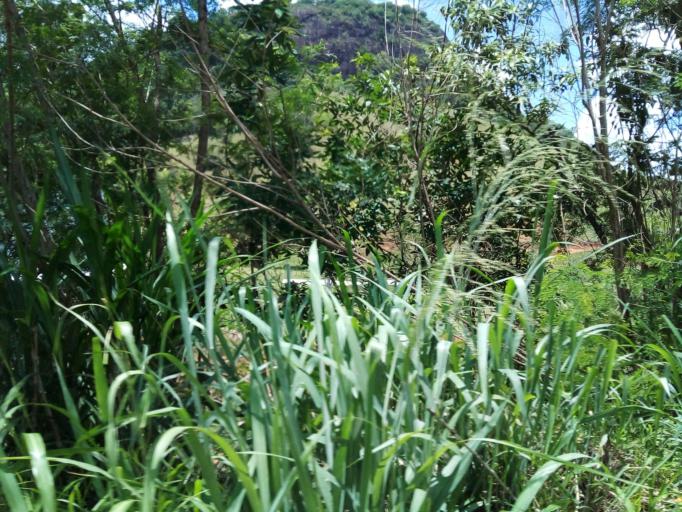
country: BR
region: Espirito Santo
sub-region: Fundao
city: Fundao
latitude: -19.9159
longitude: -40.3888
